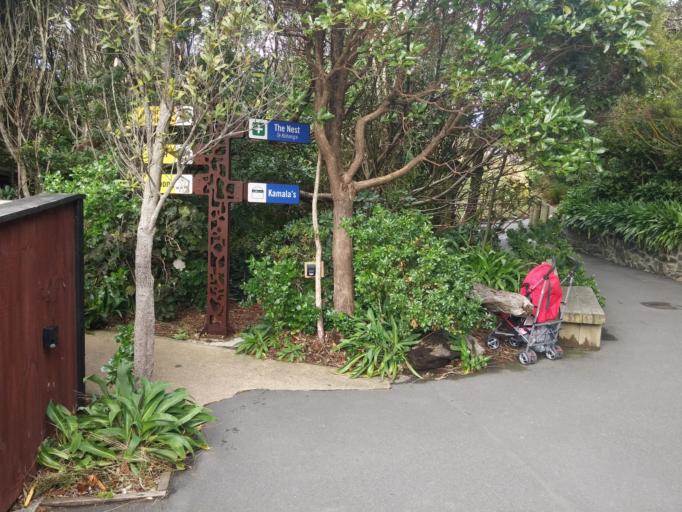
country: NZ
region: Wellington
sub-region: Wellington City
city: Wellington
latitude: -41.3199
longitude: 174.7843
